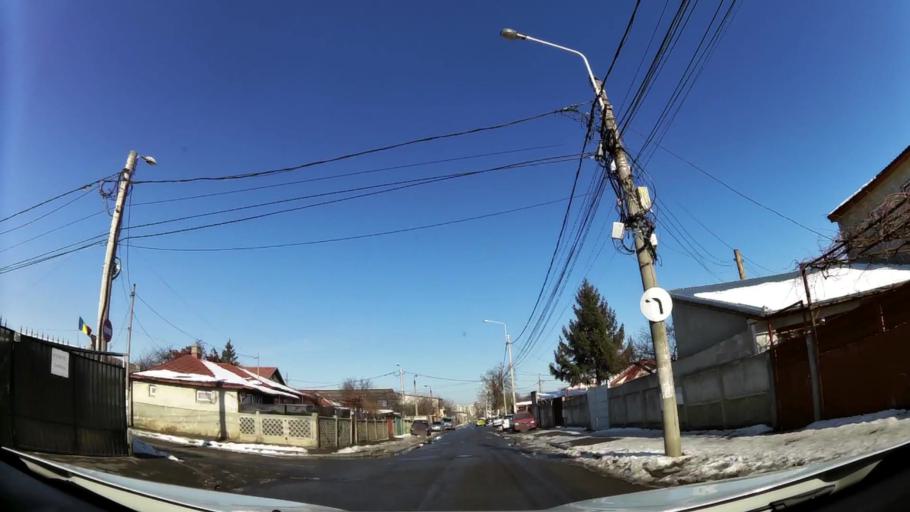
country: RO
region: Ilfov
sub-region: Comuna Magurele
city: Magurele
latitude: 44.3943
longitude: 26.0546
